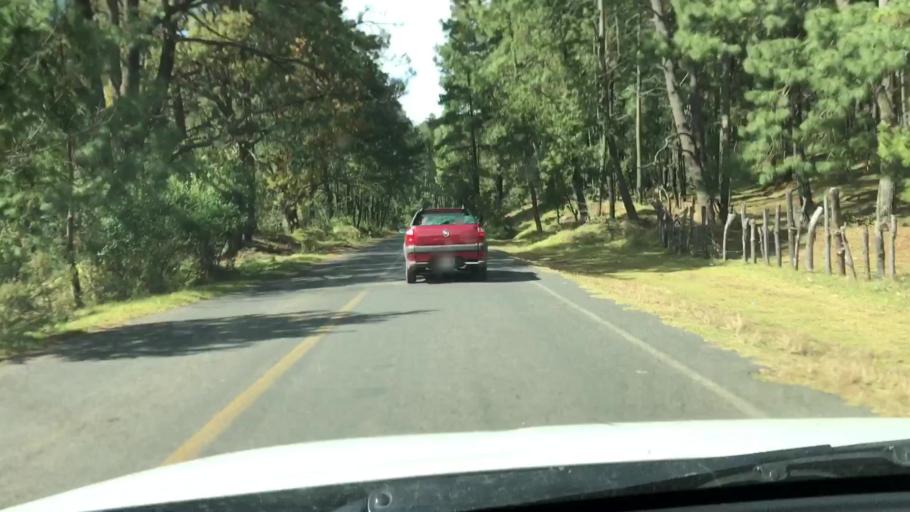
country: MX
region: Jalisco
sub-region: Amacueca
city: Tepec
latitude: 20.0527
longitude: -103.6971
